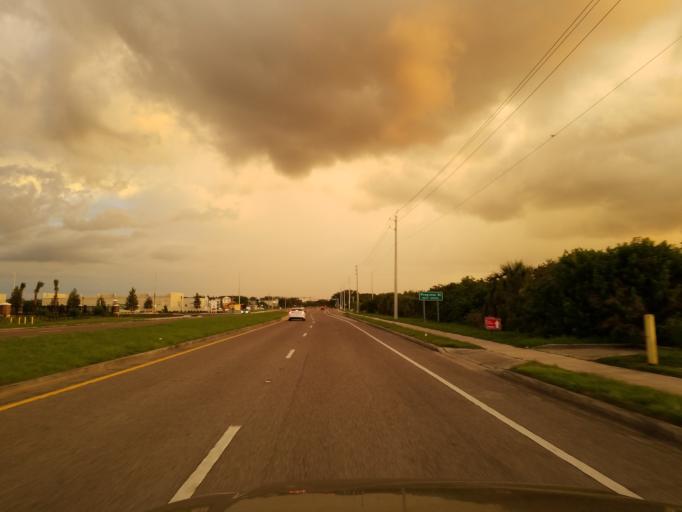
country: US
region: Florida
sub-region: Hillsborough County
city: Progress Village
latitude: 27.9021
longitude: -82.3566
